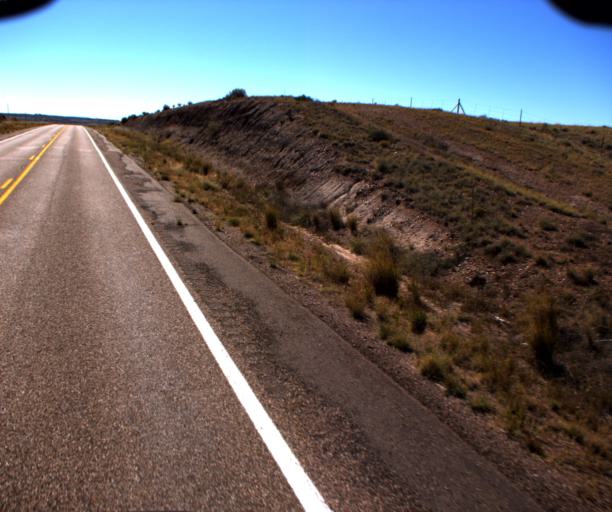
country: US
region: Arizona
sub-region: Apache County
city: Saint Johns
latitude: 34.5219
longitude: -109.4540
